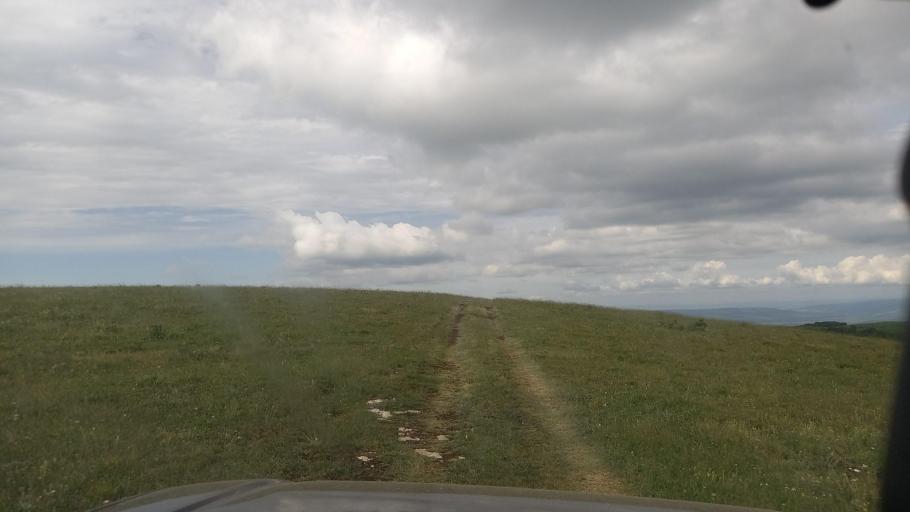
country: RU
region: Karachayevo-Cherkesiya
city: Pregradnaya
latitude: 44.0036
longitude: 41.2751
